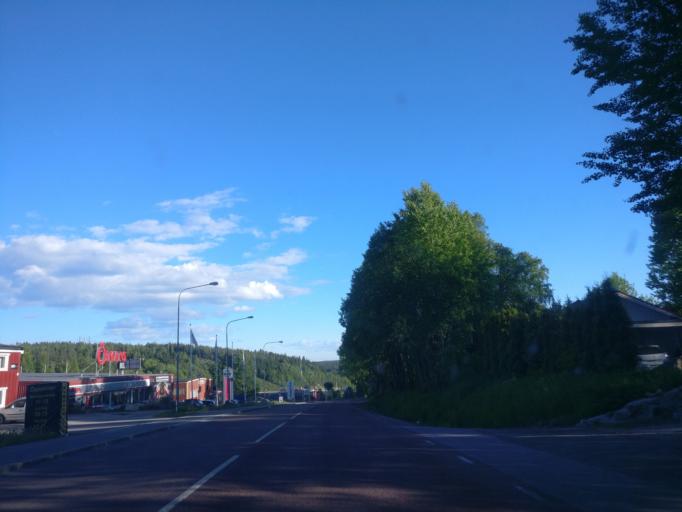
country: SE
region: Vaesternorrland
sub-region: Sundsvalls Kommun
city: Johannedal
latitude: 62.4266
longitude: 17.3467
